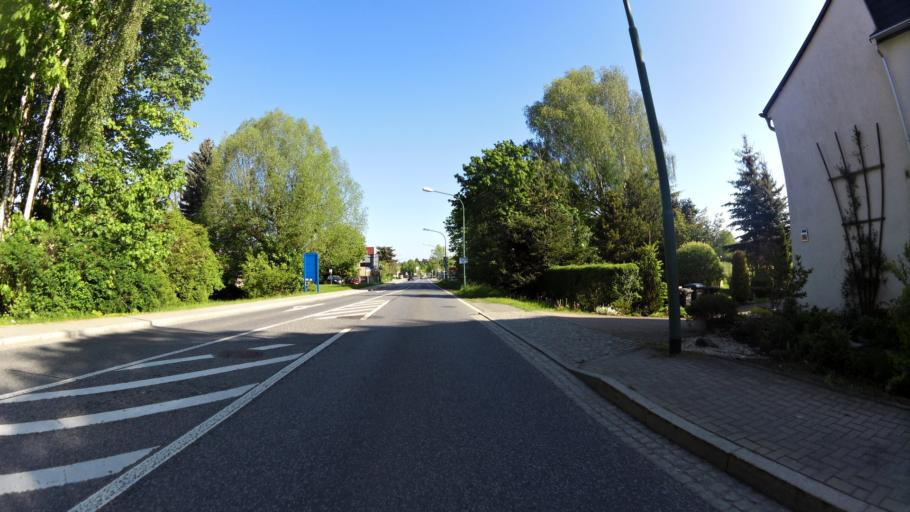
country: DE
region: Saxony
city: Neustadt in Sachsen
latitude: 51.0246
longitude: 14.2200
